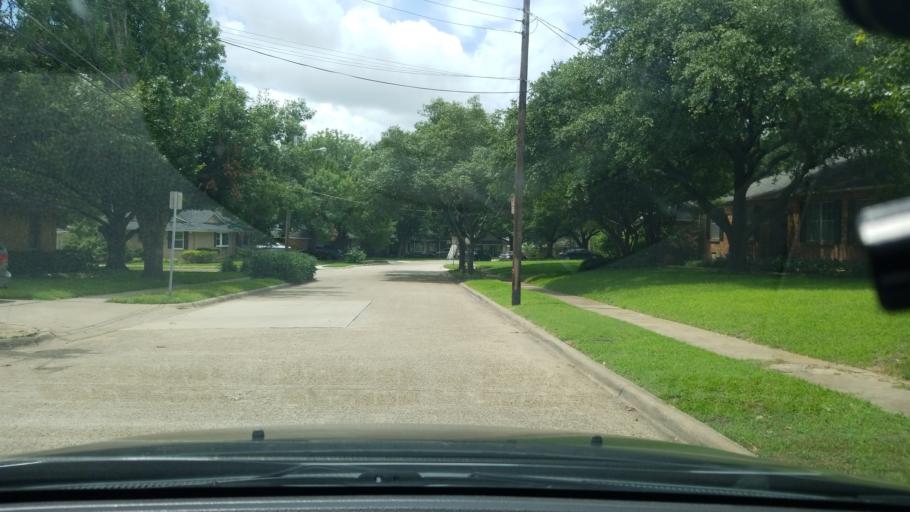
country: US
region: Texas
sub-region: Dallas County
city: Garland
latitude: 32.8262
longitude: -96.6820
